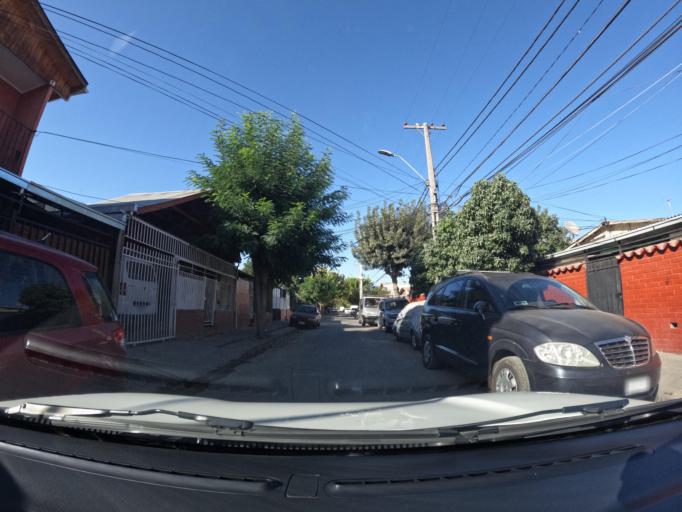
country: CL
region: Santiago Metropolitan
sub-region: Provincia de Santiago
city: Villa Presidente Frei, Nunoa, Santiago, Chile
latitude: -33.5015
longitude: -70.5725
